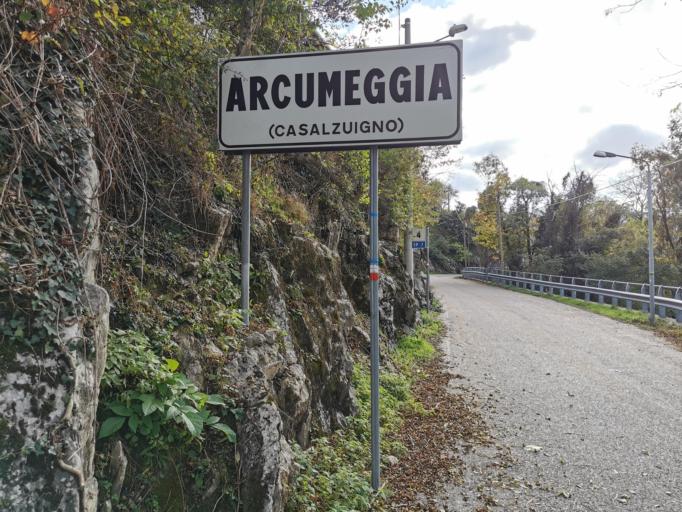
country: IT
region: Lombardy
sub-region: Provincia di Varese
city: Casalzuigno
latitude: 45.9190
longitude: 8.7147
